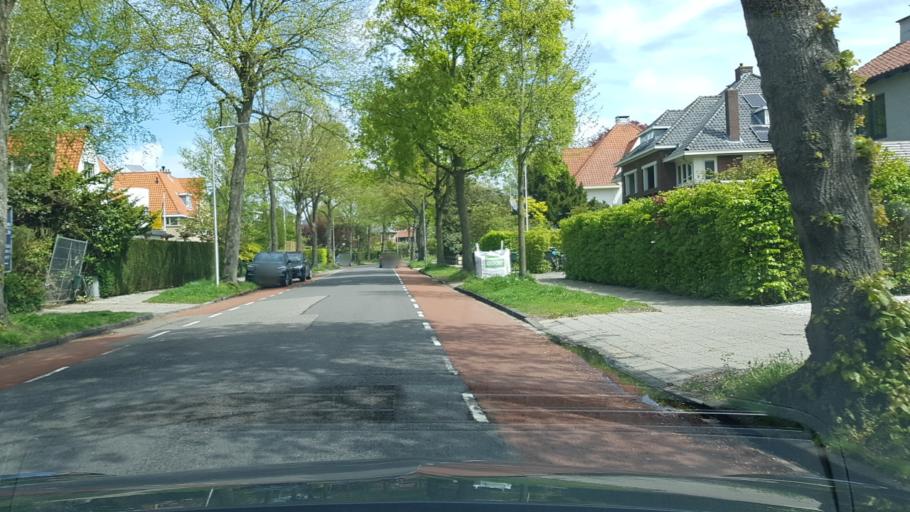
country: NL
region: North Holland
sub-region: Gemeente Heemstede
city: Heemstede
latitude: 52.3583
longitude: 4.5996
